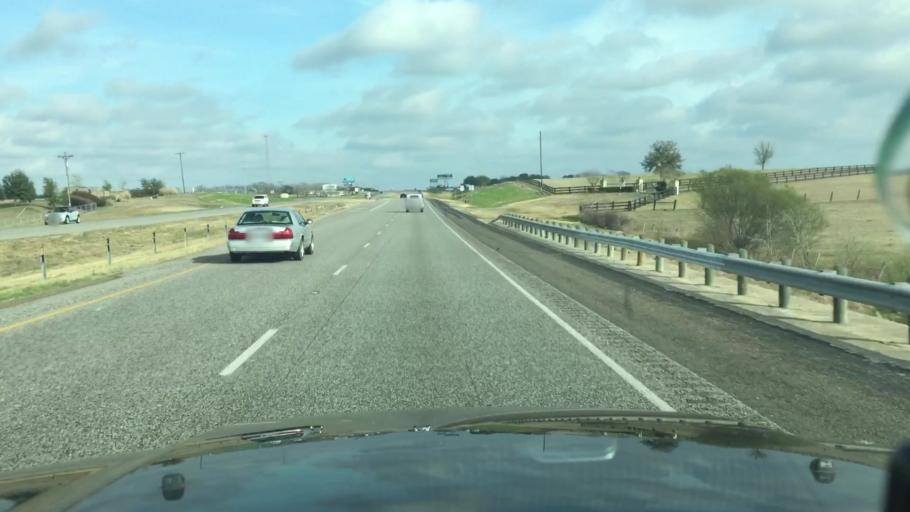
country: US
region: Texas
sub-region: Washington County
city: Brenham
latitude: 30.1395
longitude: -96.3073
